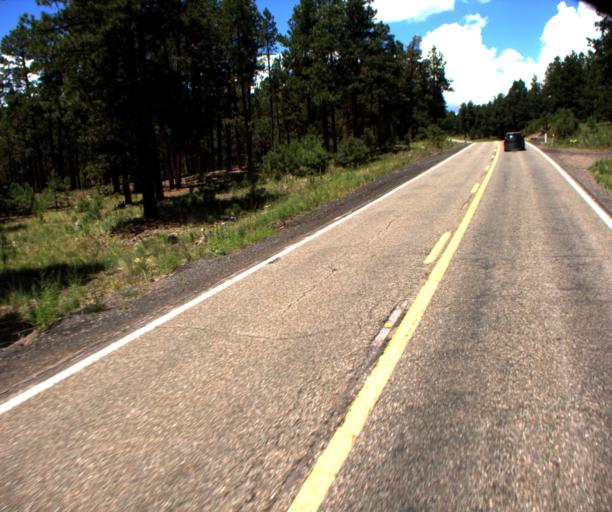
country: US
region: Arizona
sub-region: Coconino County
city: Flagstaff
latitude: 35.3024
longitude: -111.7676
